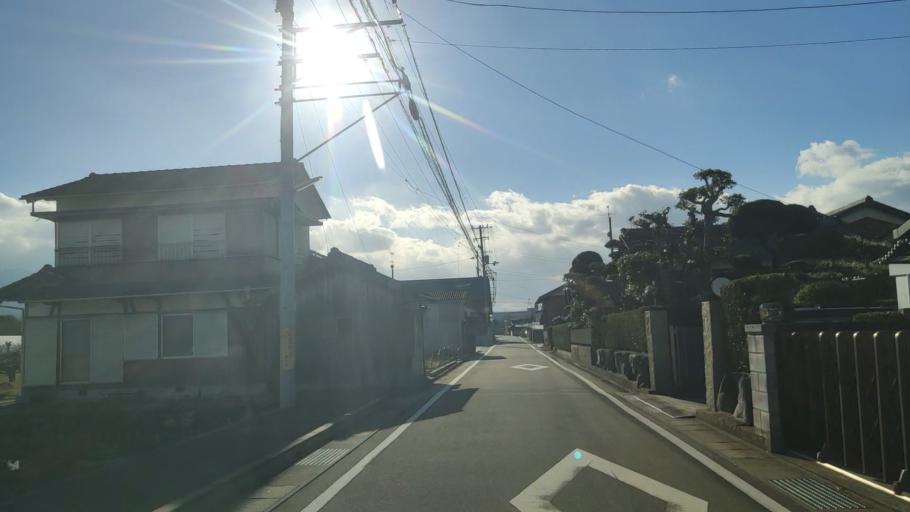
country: JP
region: Ehime
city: Saijo
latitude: 33.9146
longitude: 133.1023
